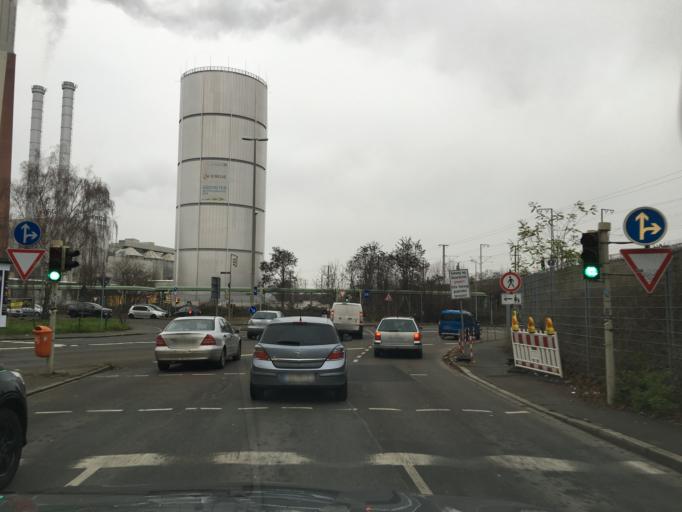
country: DE
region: Bavaria
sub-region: Regierungsbezirk Mittelfranken
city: Nuernberg
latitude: 49.4409
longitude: 11.0635
